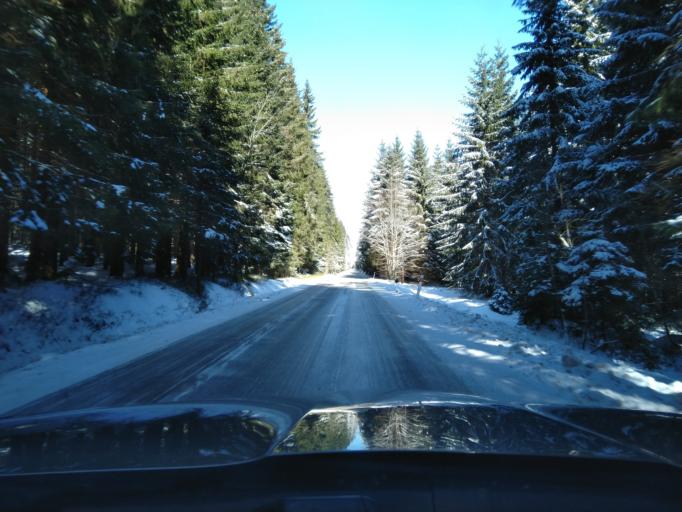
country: CZ
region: Jihocesky
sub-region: Okres Prachatice
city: Zdikov
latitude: 49.0499
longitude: 13.6623
